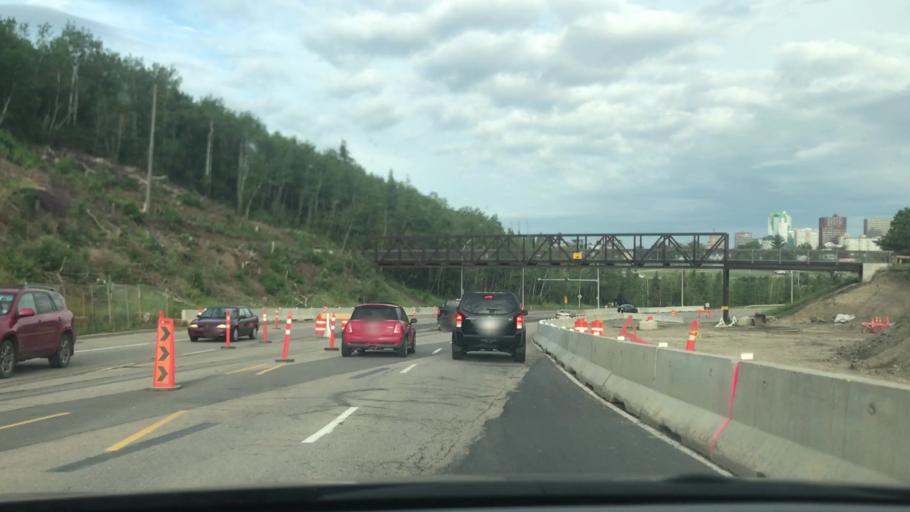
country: CA
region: Alberta
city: Edmonton
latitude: 53.5331
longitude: -113.4787
